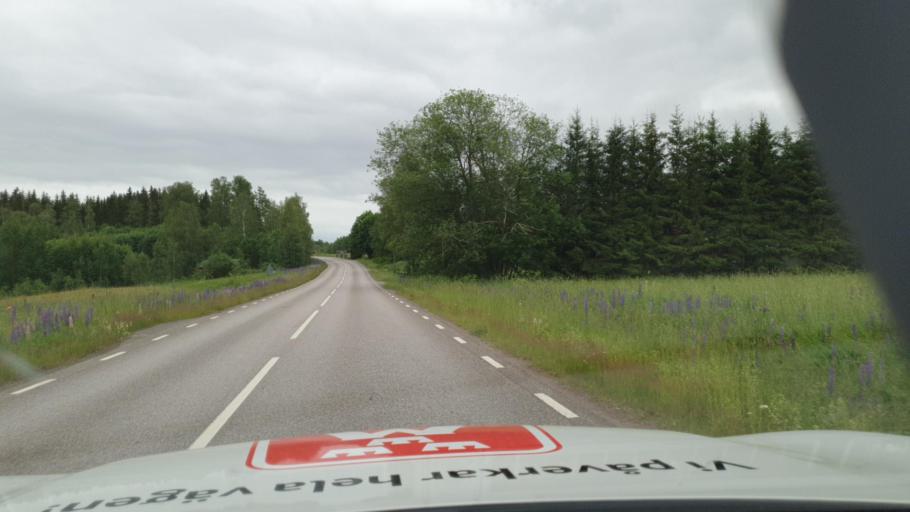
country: SE
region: Vaermland
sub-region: Sunne Kommun
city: Sunne
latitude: 59.7944
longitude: 13.0705
